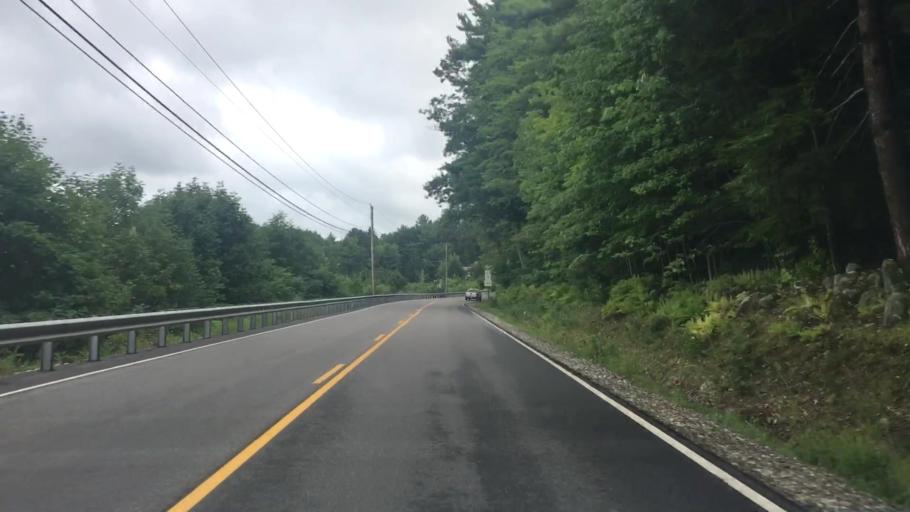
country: US
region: Maine
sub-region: York County
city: Limerick
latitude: 43.6940
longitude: -70.7981
